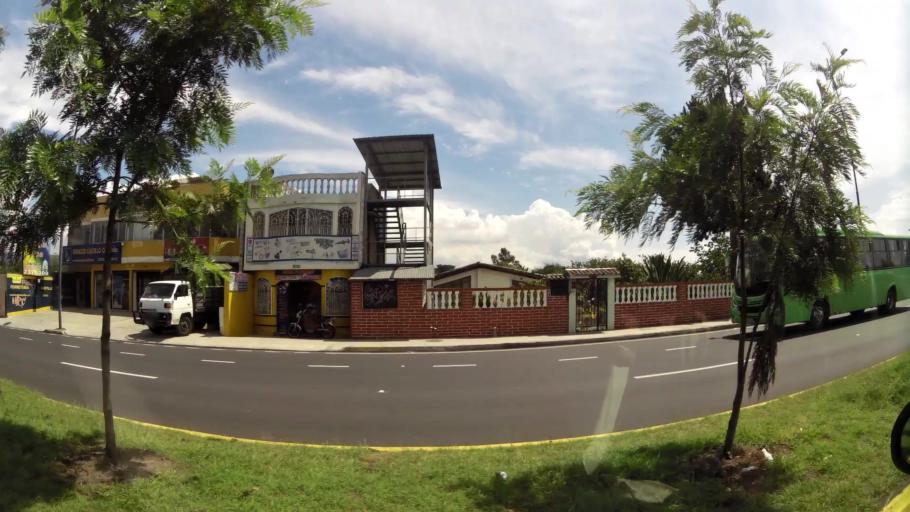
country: EC
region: Pichincha
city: Sangolqui
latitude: -0.2133
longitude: -78.3886
